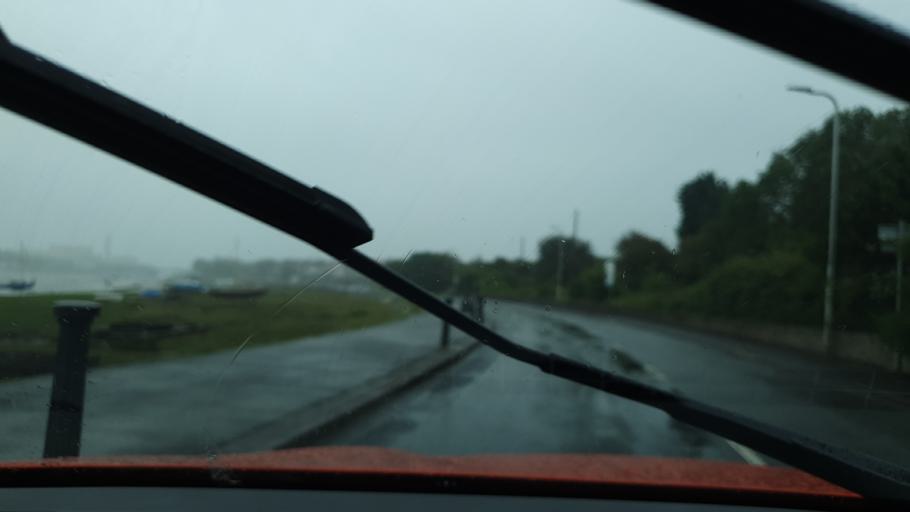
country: GB
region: England
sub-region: Cumbria
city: Barrow in Furness
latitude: 54.1163
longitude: -3.2512
